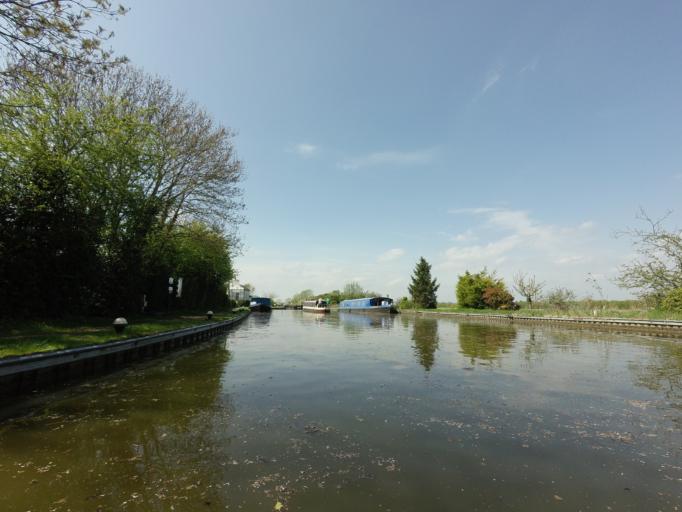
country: GB
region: England
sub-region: Buckinghamshire
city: Cheddington
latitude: 51.8729
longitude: -0.6511
